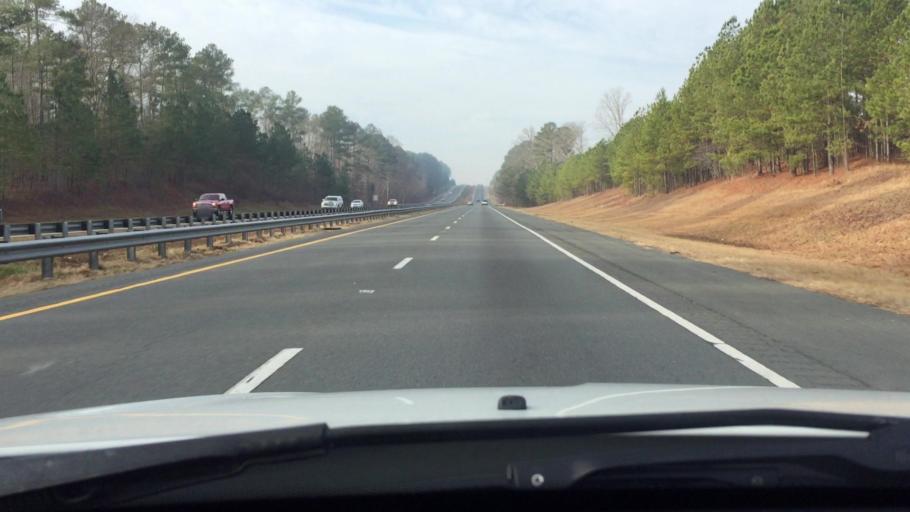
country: US
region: North Carolina
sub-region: Chatham County
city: Pittsboro
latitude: 35.6395
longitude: -79.0355
